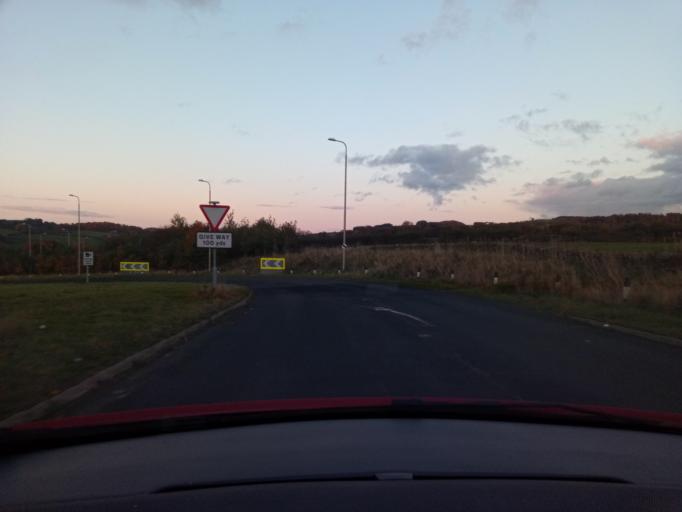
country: GB
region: England
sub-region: Northumberland
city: Warden
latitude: 54.9721
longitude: -2.2365
